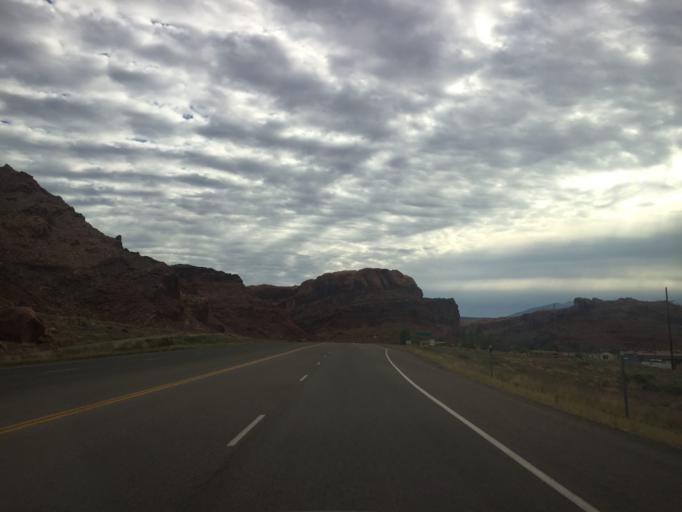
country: US
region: Utah
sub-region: Grand County
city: Moab
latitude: 38.6052
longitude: -109.5955
